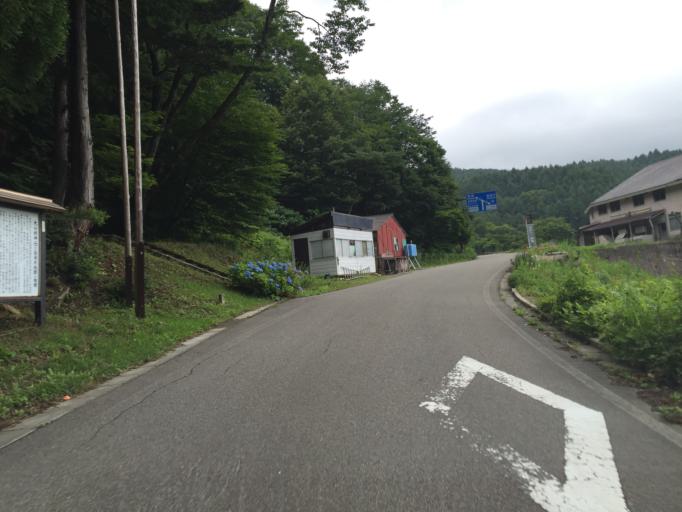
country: JP
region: Fukushima
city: Inawashiro
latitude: 37.6430
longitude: 140.2221
